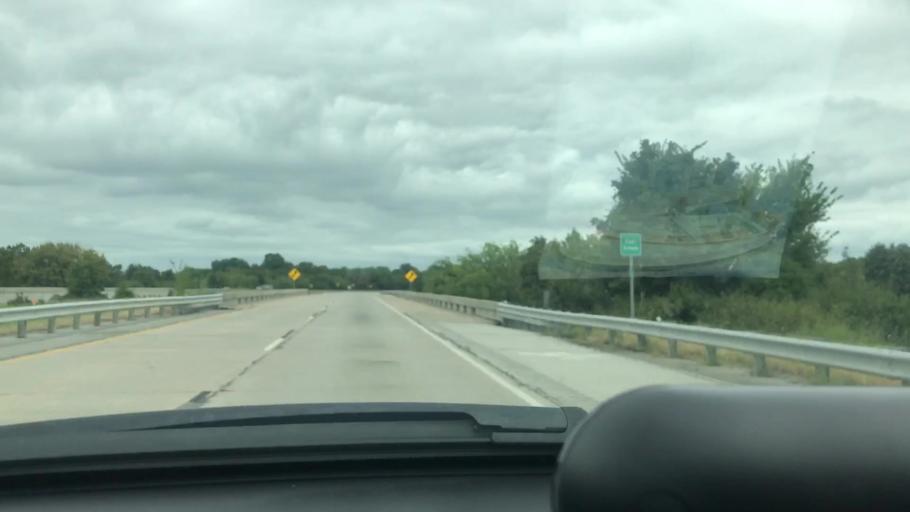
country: US
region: Oklahoma
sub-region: Wagoner County
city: Wagoner
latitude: 35.9079
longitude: -95.4026
